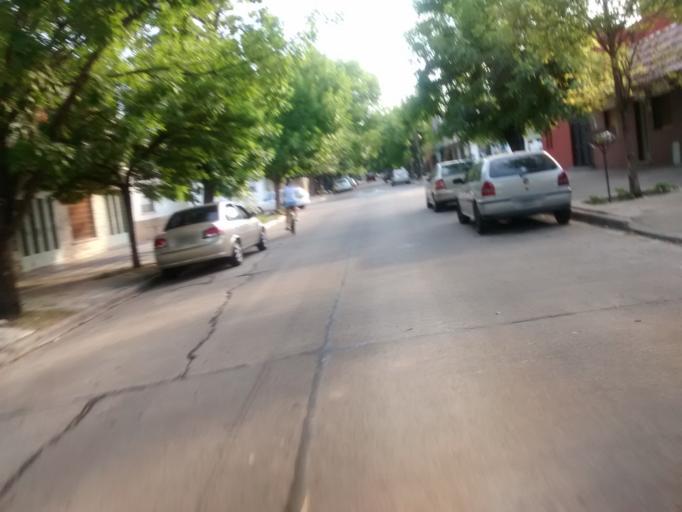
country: AR
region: Buenos Aires
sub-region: Partido de La Plata
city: La Plata
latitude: -34.9112
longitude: -57.9744
